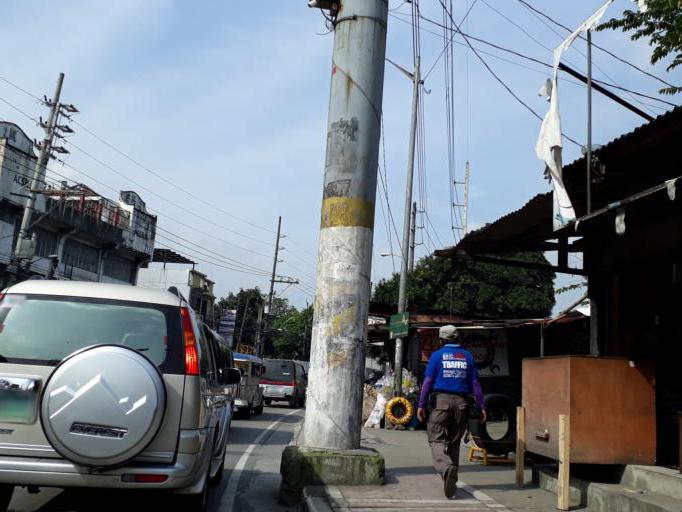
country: PH
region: Calabarzon
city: Bagong Pagasa
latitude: 14.6854
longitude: 121.0237
